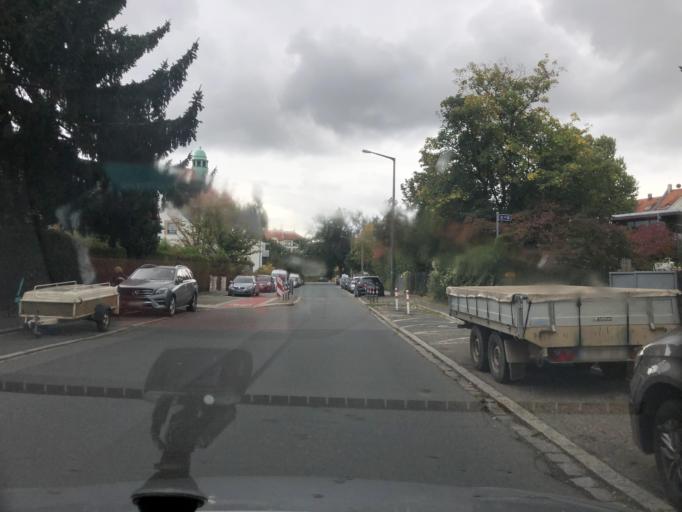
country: DE
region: Bavaria
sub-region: Regierungsbezirk Mittelfranken
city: Nuernberg
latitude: 49.4649
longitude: 11.0643
